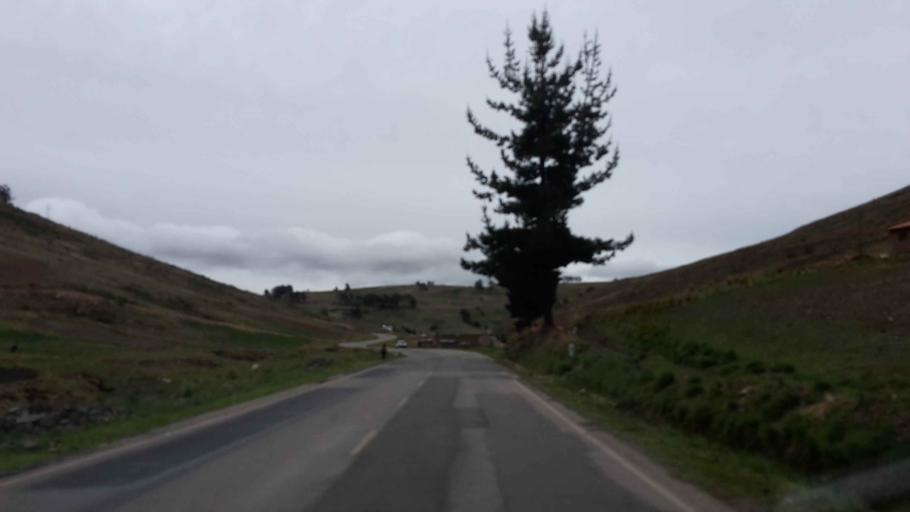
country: BO
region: Cochabamba
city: Arani
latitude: -17.4806
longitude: -65.5897
